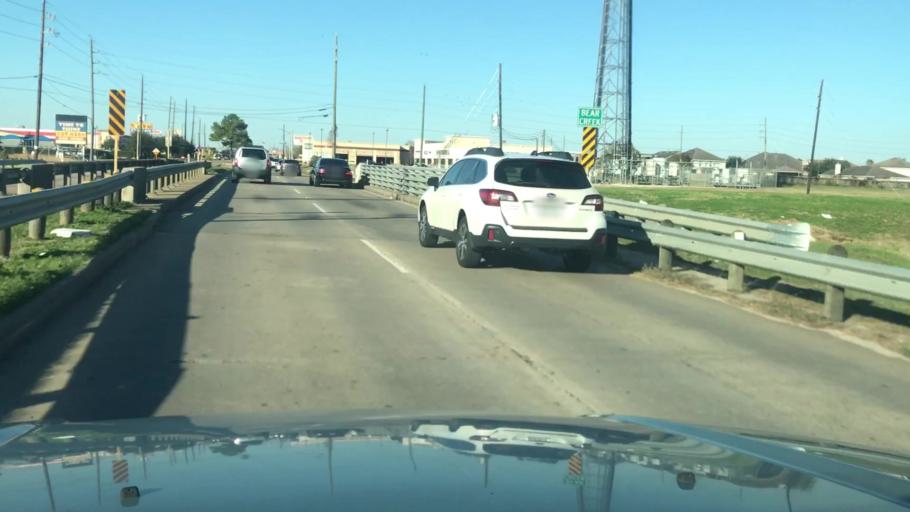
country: US
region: Texas
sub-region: Harris County
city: Oak Cliff Place
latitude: 29.8525
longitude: -95.7186
